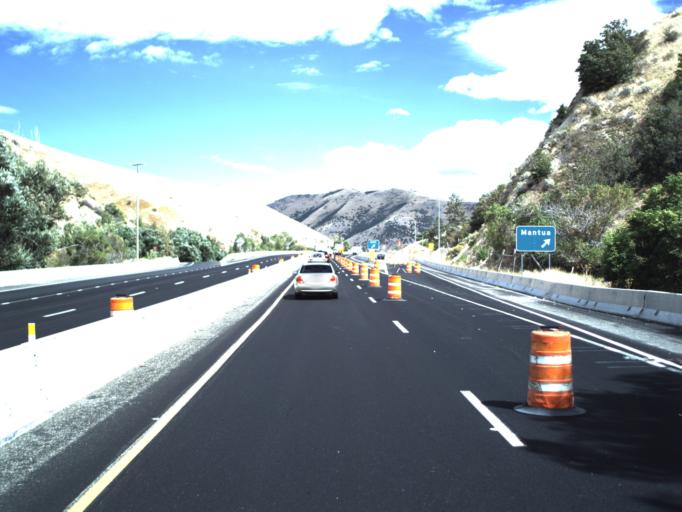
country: US
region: Utah
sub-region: Box Elder County
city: Brigham City
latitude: 41.4965
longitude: -111.9582
